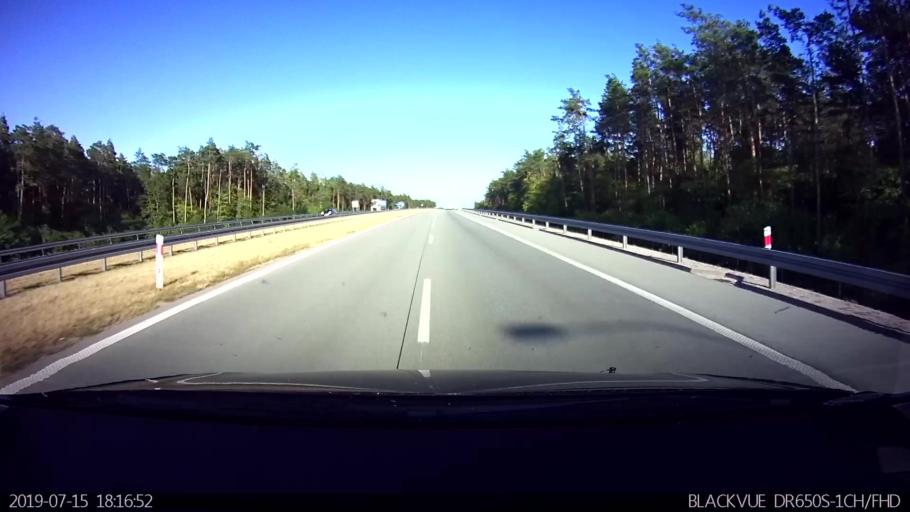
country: PL
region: Lodz Voivodeship
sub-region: Powiat zdunskowolski
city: Zdunska Wola
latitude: 51.5736
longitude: 18.9501
